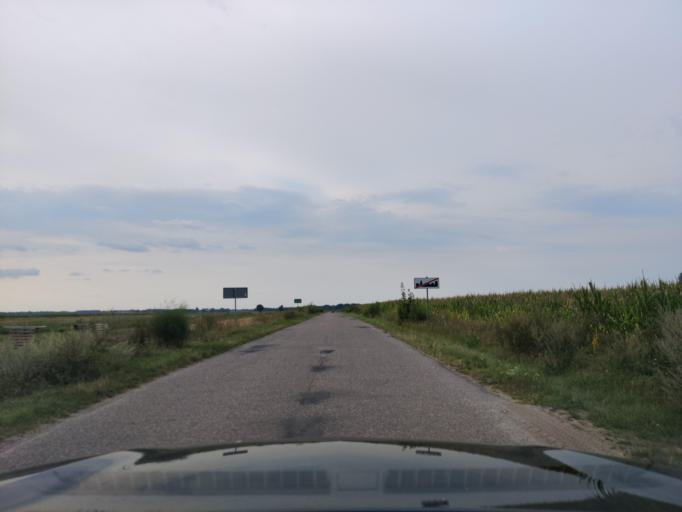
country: PL
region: Masovian Voivodeship
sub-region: Powiat pultuski
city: Obryte
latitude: 52.7171
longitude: 21.2494
